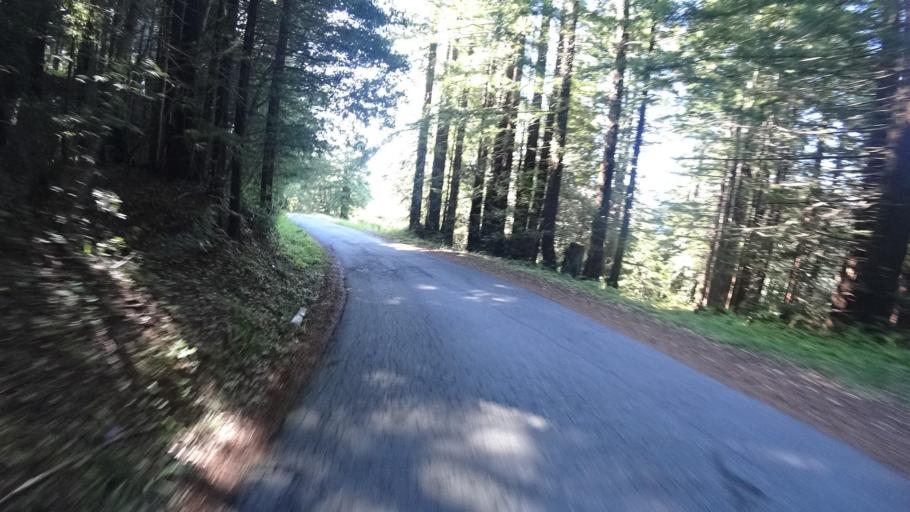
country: US
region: California
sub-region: Humboldt County
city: Rio Dell
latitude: 40.4562
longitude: -123.9951
